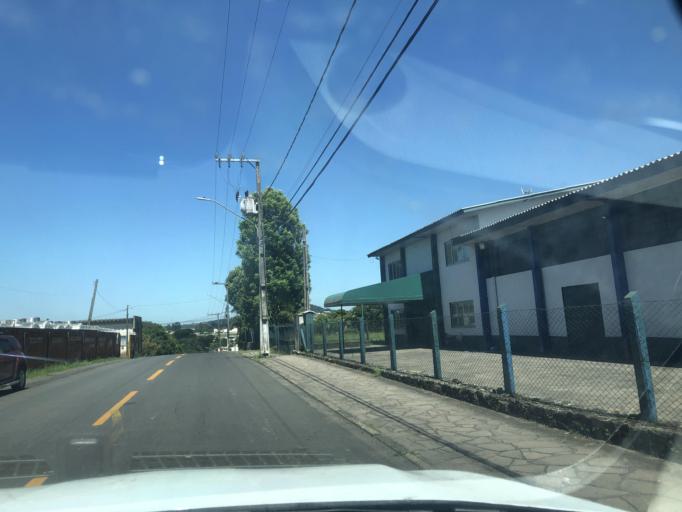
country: BR
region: Santa Catarina
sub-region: Lages
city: Lages
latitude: -27.7848
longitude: -50.3090
